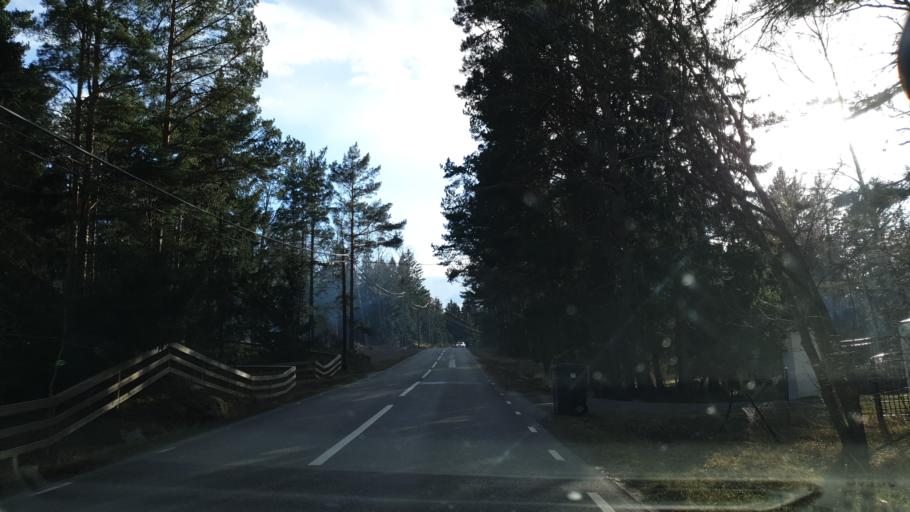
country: SE
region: Stockholm
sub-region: Varmdo Kommun
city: Holo
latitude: 59.3160
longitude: 18.7224
